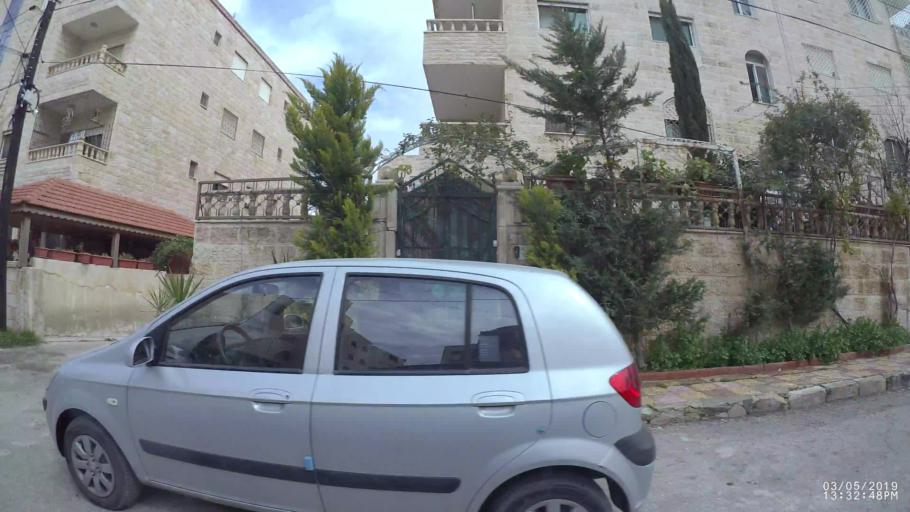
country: JO
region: Amman
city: Amman
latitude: 31.9945
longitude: 35.9434
